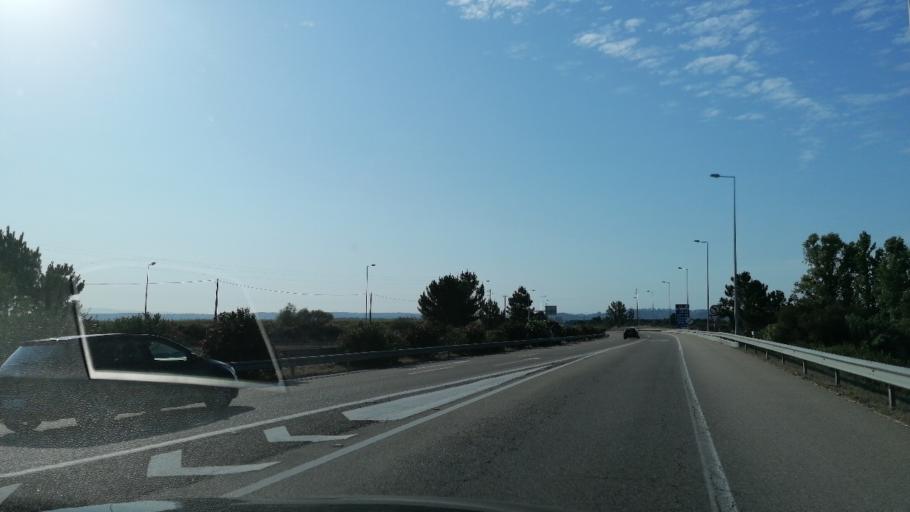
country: PT
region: Santarem
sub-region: Almeirim
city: Almeirim
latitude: 39.1797
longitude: -8.6293
